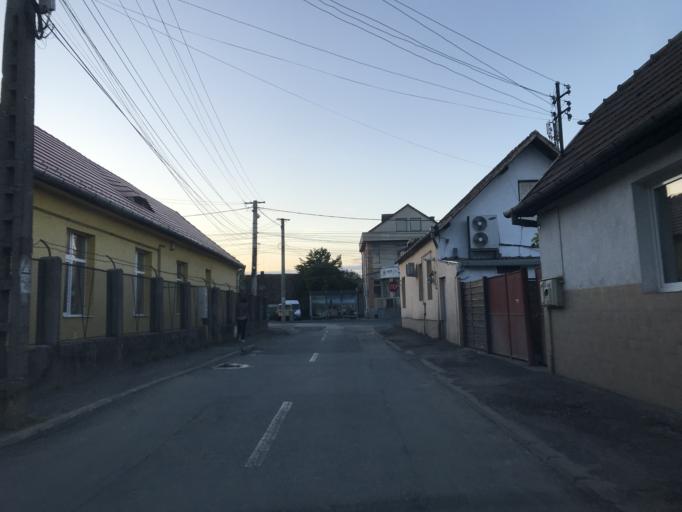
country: RO
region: Sibiu
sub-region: Municipiul Sibiu
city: Sibiu
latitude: 45.7998
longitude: 24.1669
